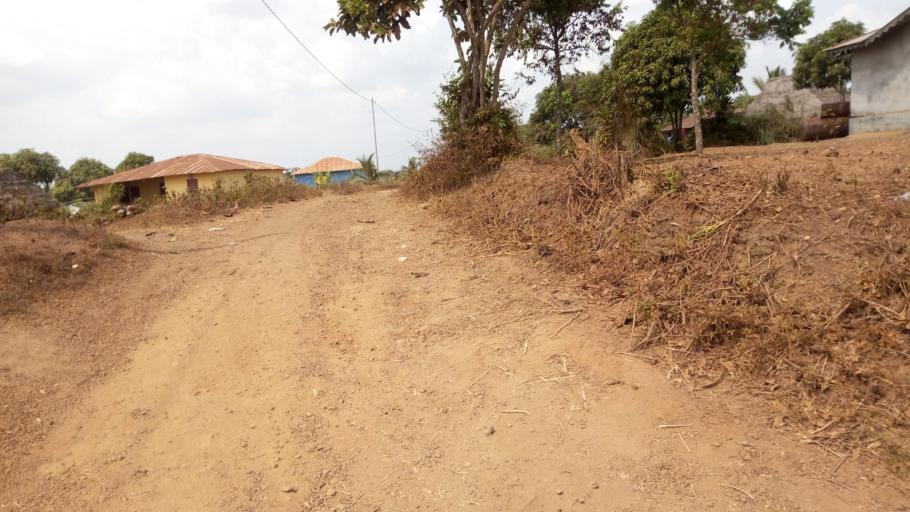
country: SL
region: Southern Province
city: Mogbwemo
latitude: 7.7877
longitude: -12.3078
